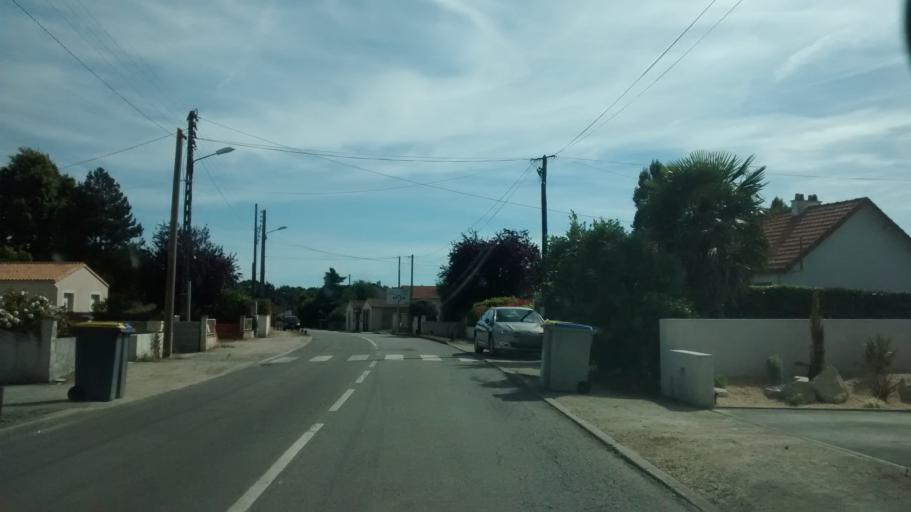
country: FR
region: Pays de la Loire
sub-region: Departement de la Loire-Atlantique
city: Pont-Saint-Martin
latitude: 47.1266
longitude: -1.6177
